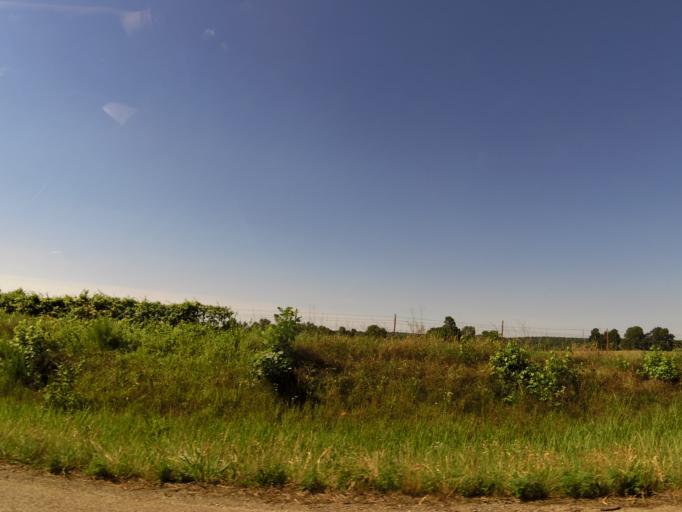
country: US
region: Arkansas
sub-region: Clay County
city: Piggott
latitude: 36.4291
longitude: -90.2457
